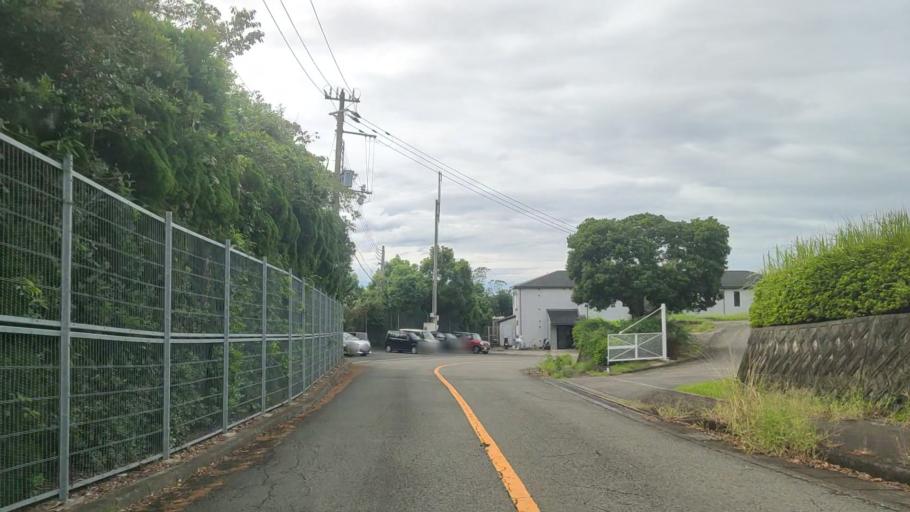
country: JP
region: Wakayama
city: Tanabe
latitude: 33.6677
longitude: 135.3702
